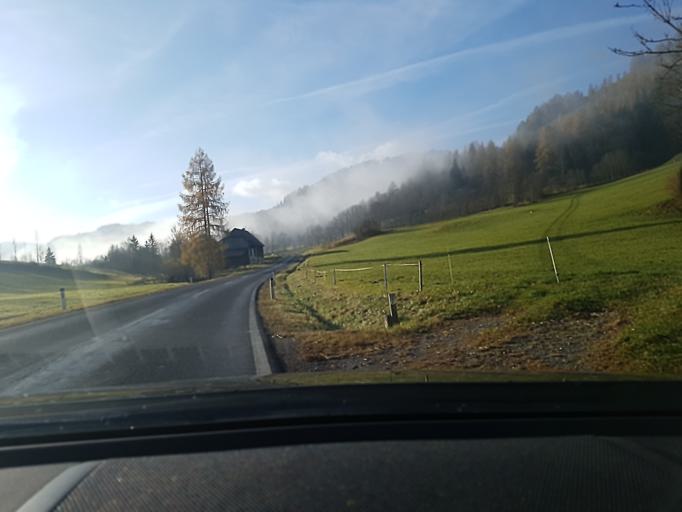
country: AT
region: Styria
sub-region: Politischer Bezirk Murau
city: Schoder
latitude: 47.1745
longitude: 14.1139
